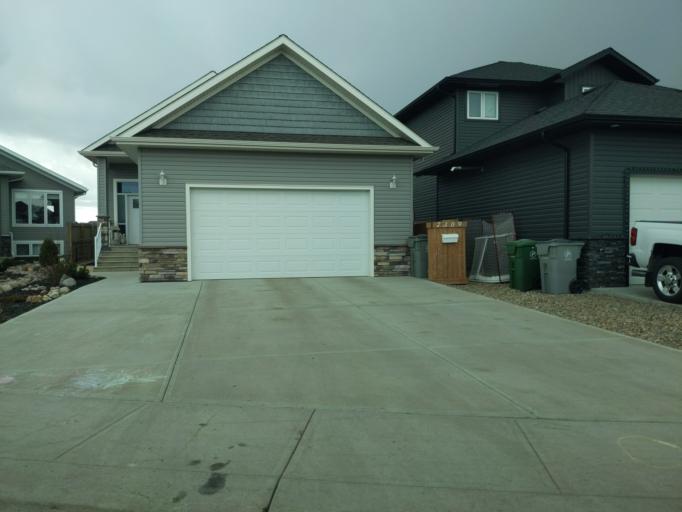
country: CA
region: Saskatchewan
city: Lloydminster
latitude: 53.2703
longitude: -110.0520
